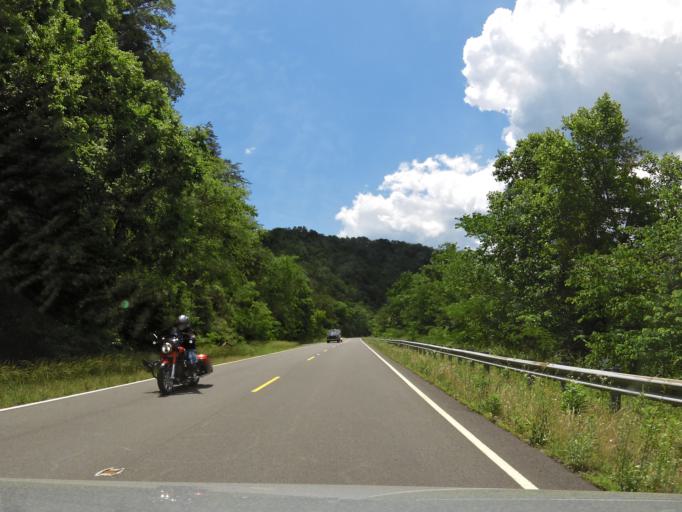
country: US
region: Tennessee
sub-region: Loudon County
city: Greenback
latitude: 35.5336
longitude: -83.9921
